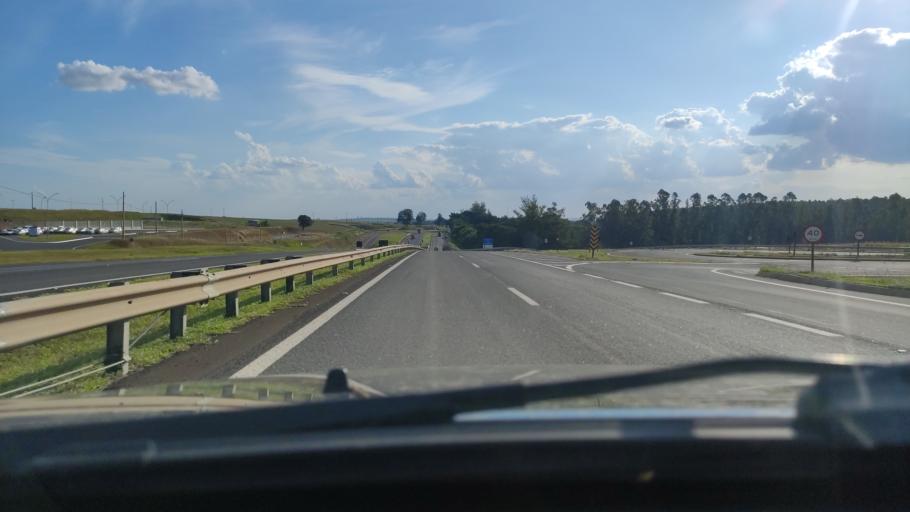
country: BR
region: Sao Paulo
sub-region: Itapira
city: Itapira
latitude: -22.4511
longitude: -46.8512
